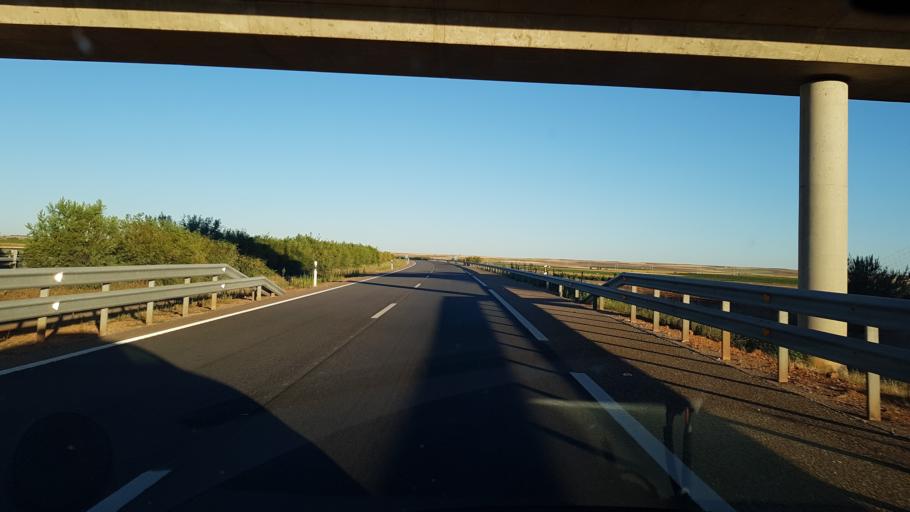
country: ES
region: Castille and Leon
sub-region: Provincia de Zamora
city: Morales de Toro
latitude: 41.5450
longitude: -5.3043
